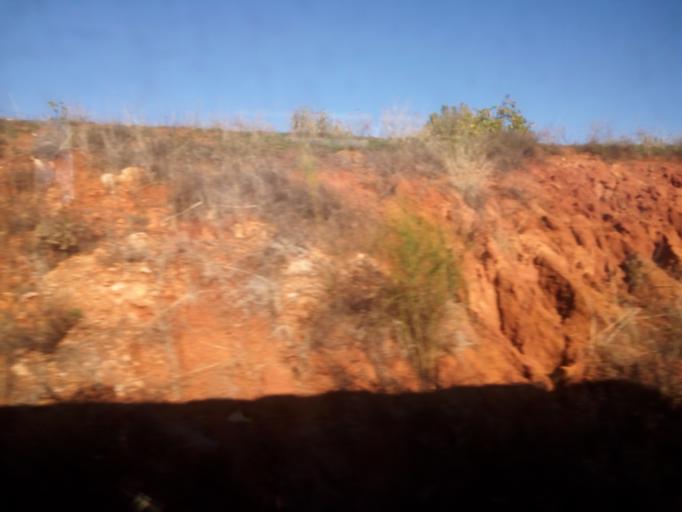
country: PT
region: Faro
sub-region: Loule
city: Almancil
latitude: 37.1006
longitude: -8.0480
